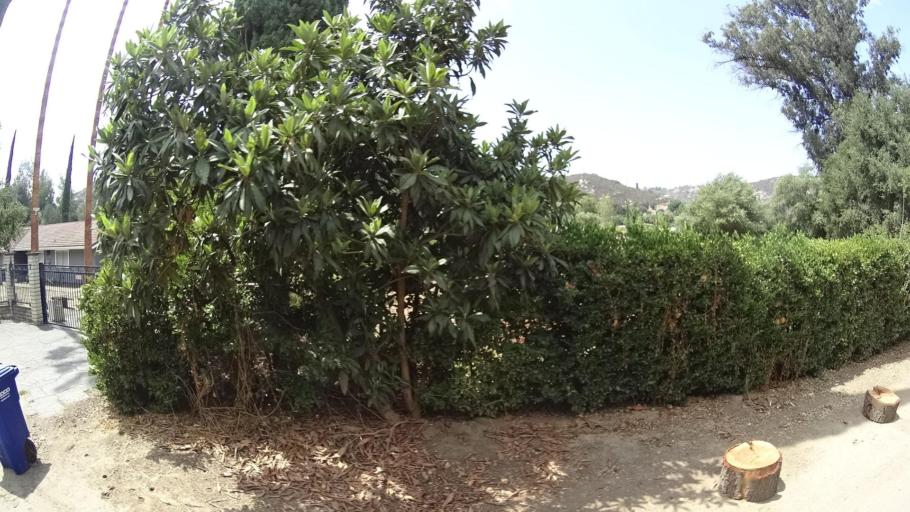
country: US
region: California
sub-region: San Diego County
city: Hidden Meadows
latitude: 33.2043
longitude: -117.0893
